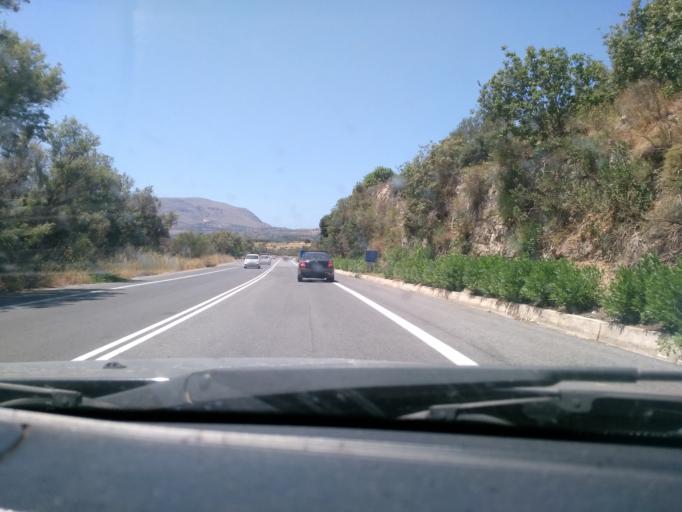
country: GR
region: Crete
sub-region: Nomos Chanias
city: Kalivai
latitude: 35.4280
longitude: 24.1699
